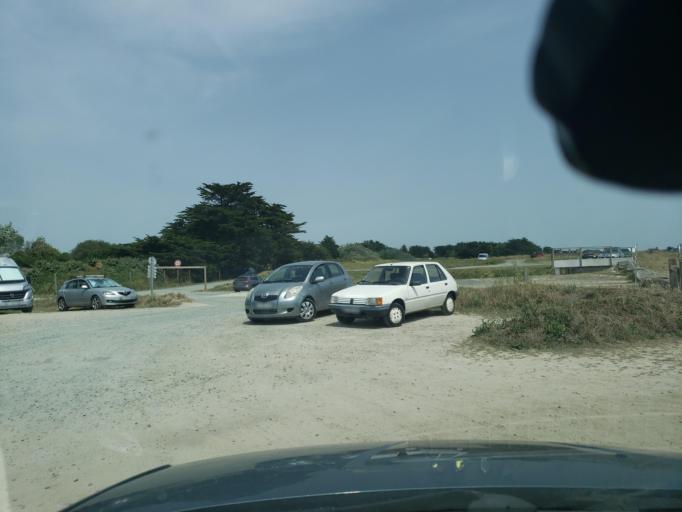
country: FR
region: Brittany
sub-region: Departement du Finistere
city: Guilvinec
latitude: 47.8003
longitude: -4.3184
